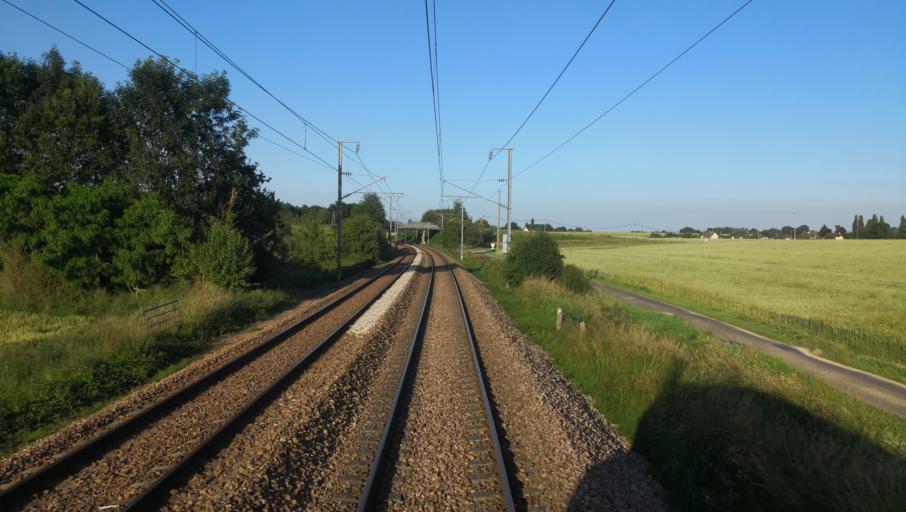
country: FR
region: Haute-Normandie
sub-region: Departement de l'Eure
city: Thiberville
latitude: 49.0809
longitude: 0.4991
